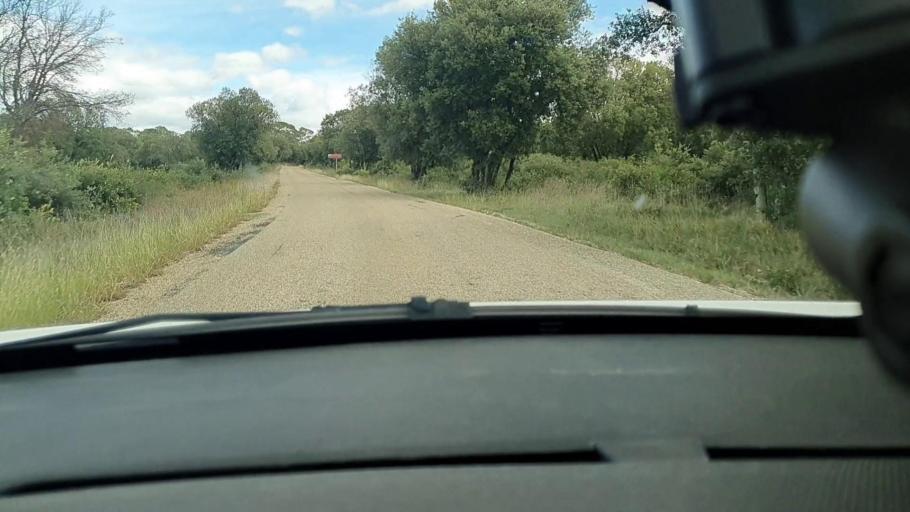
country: FR
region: Languedoc-Roussillon
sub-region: Departement du Gard
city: Salindres
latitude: 44.1658
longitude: 4.2469
